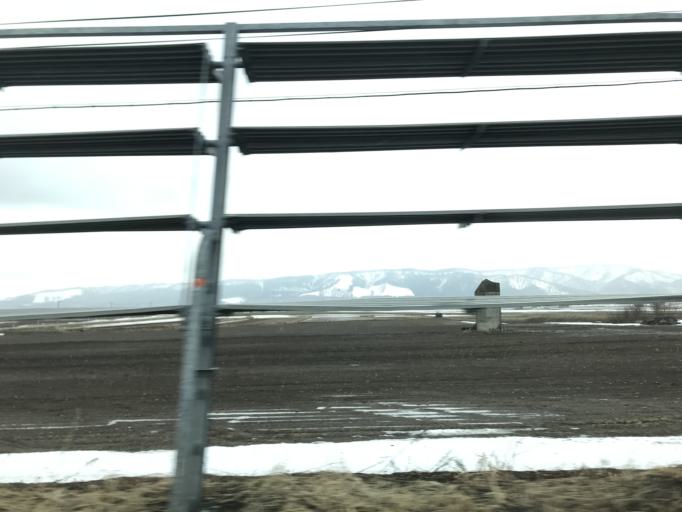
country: JP
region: Hokkaido
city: Nayoro
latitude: 44.2267
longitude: 142.3948
